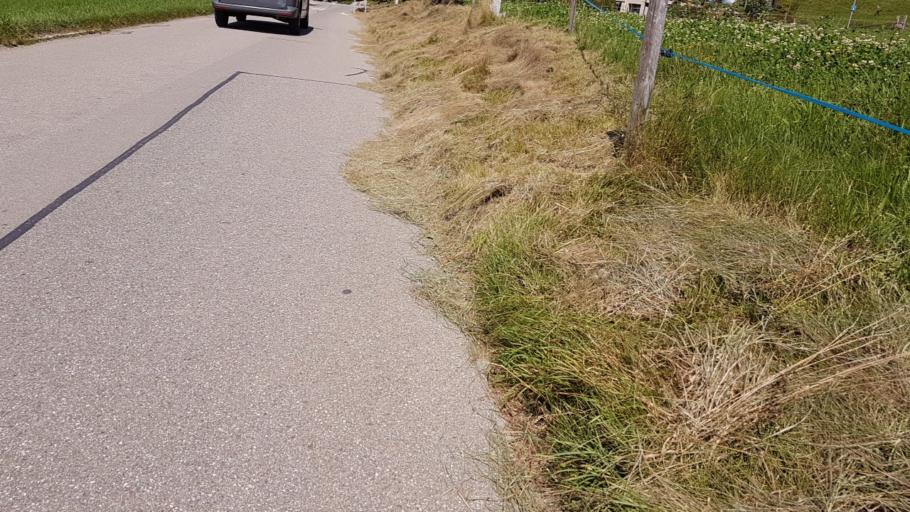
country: CH
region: Bern
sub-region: Bern-Mittelland District
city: Konolfingen
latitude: 46.8648
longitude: 7.6289
